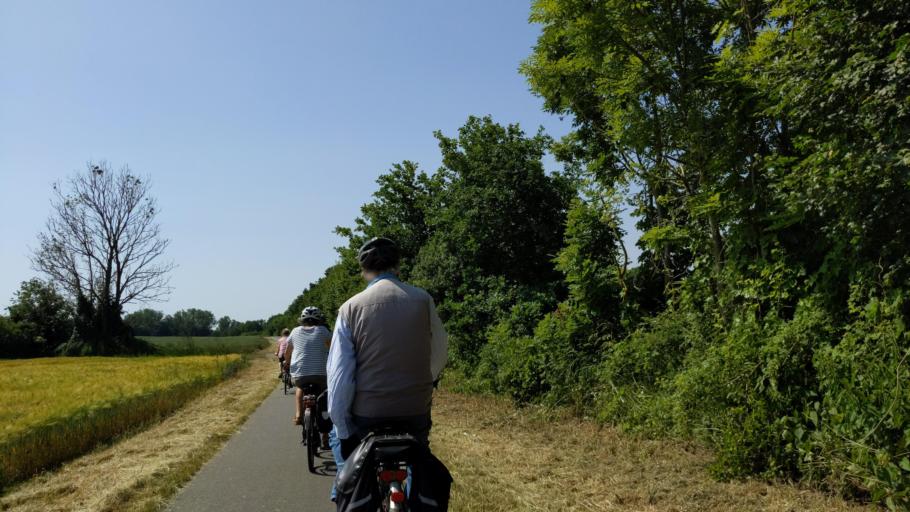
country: DE
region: Schleswig-Holstein
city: Berkenthin
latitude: 53.7454
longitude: 10.6551
